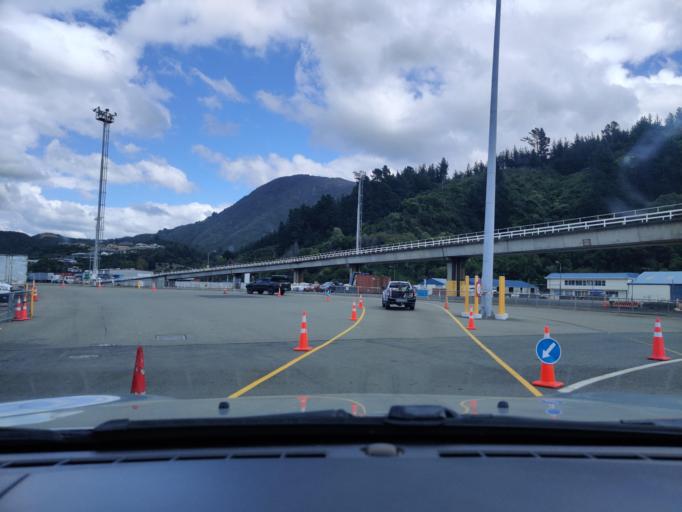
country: NZ
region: Marlborough
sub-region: Marlborough District
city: Picton
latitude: -41.2852
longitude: 174.0050
